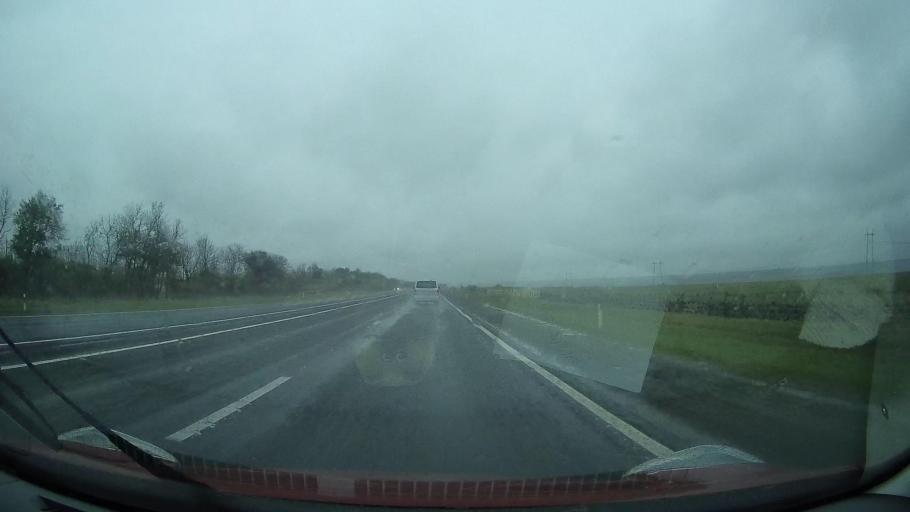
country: RU
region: Stavropol'skiy
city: Nevinnomyssk
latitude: 44.6121
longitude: 42.1190
